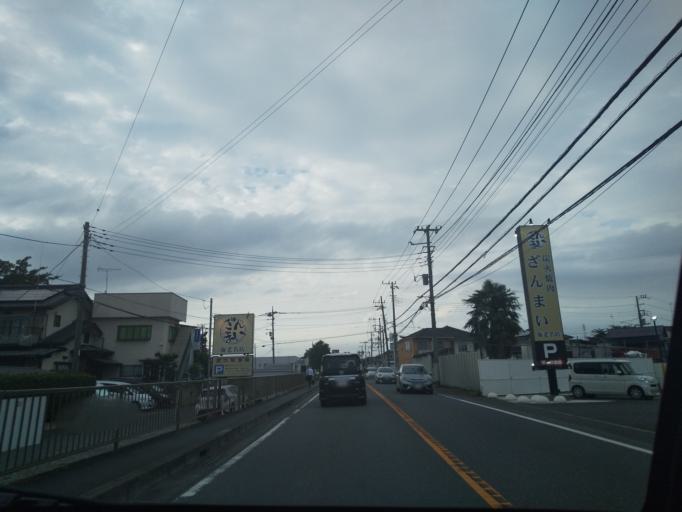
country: JP
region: Kanagawa
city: Zama
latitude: 35.4701
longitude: 139.3888
